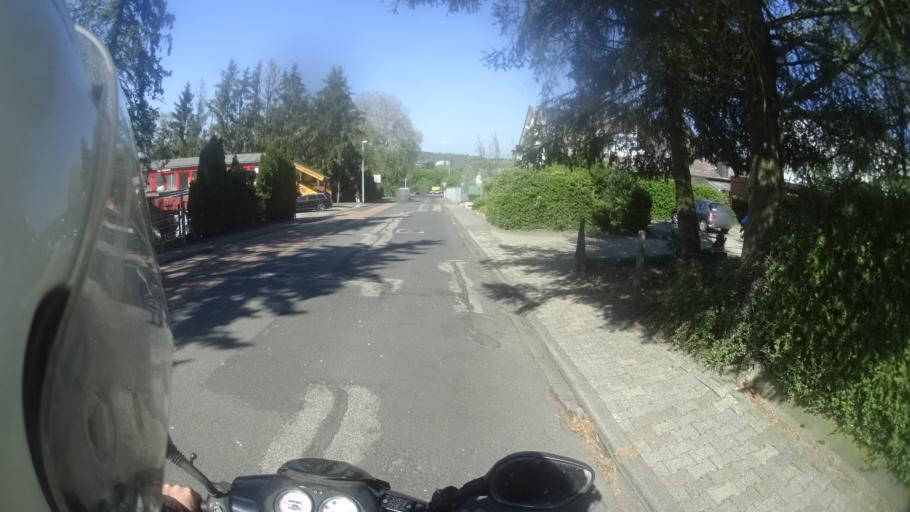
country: DE
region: Hesse
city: Taunusstein
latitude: 50.1359
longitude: 8.1488
